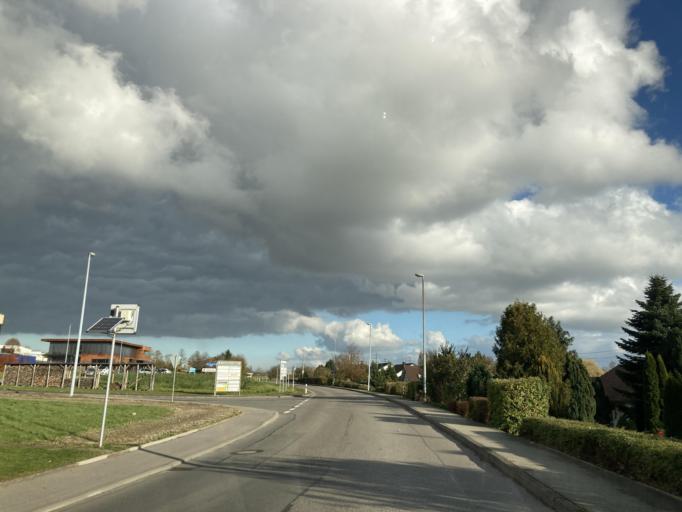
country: DE
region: Baden-Wuerttemberg
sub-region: Karlsruhe Region
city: Empfingen
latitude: 48.3947
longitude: 8.7147
